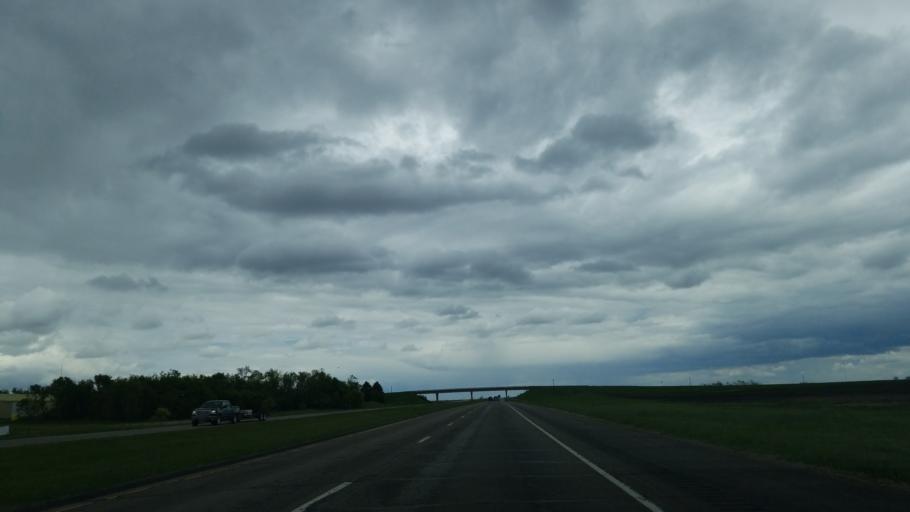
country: US
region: North Dakota
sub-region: Barnes County
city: Valley City
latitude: 46.9068
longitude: -98.2751
